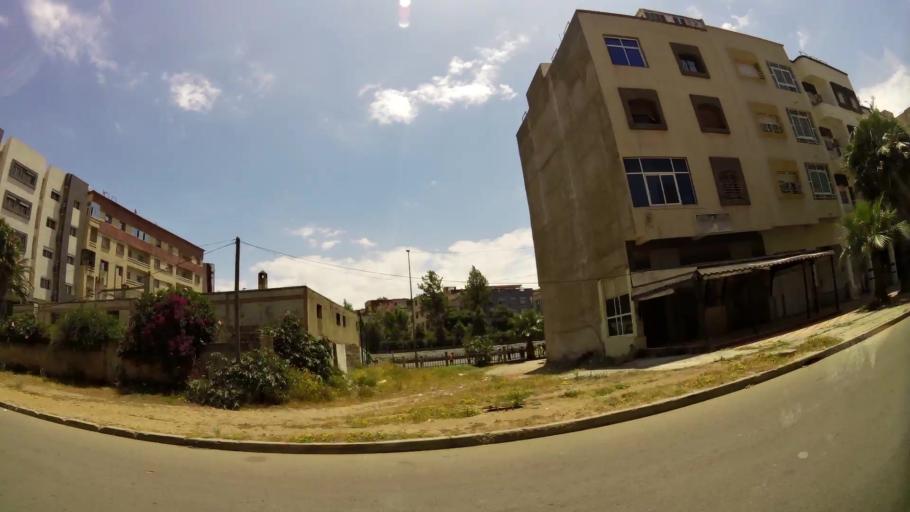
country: MA
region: Gharb-Chrarda-Beni Hssen
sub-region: Kenitra Province
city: Kenitra
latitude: 34.2551
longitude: -6.6092
